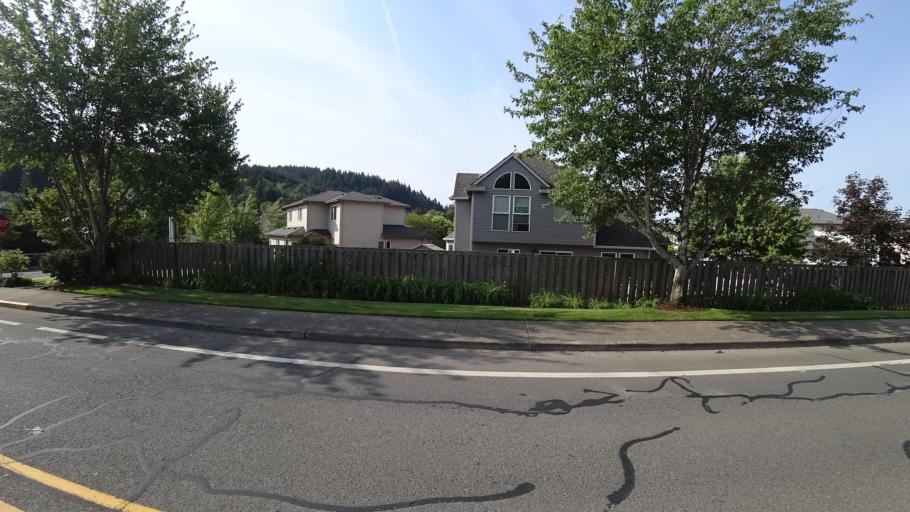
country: US
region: Oregon
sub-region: Clackamas County
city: Happy Valley
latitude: 45.4540
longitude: -122.5147
